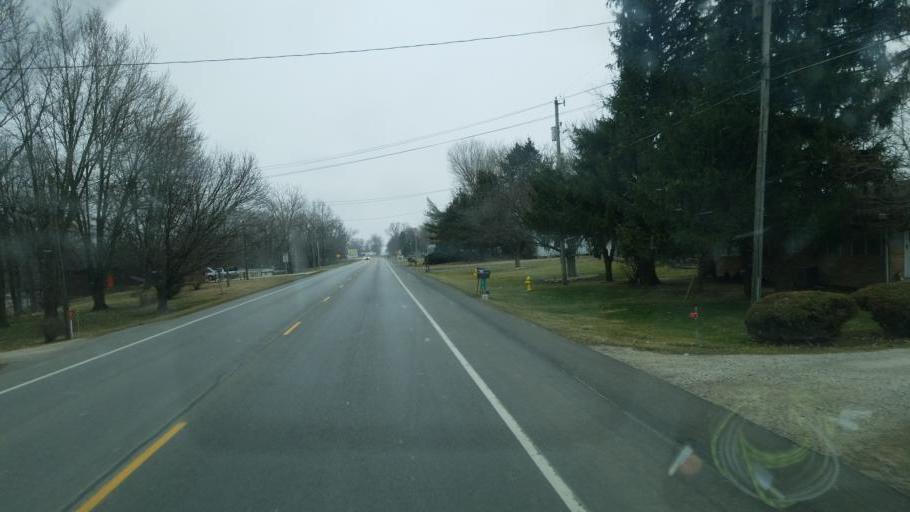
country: US
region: Indiana
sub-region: Wabash County
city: Wabash
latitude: 40.7732
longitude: -85.8195
